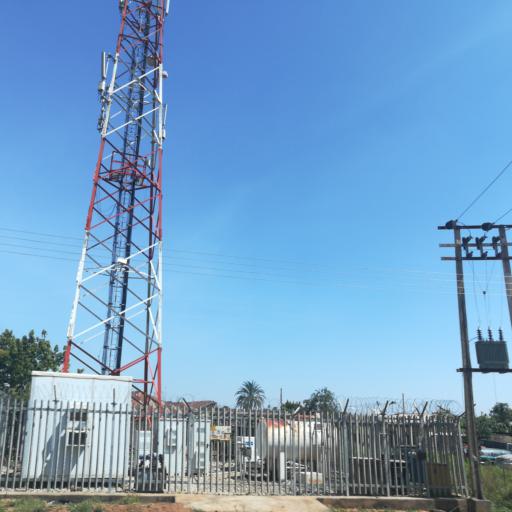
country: NG
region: Plateau
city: Bukuru
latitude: 9.7871
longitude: 8.8781
